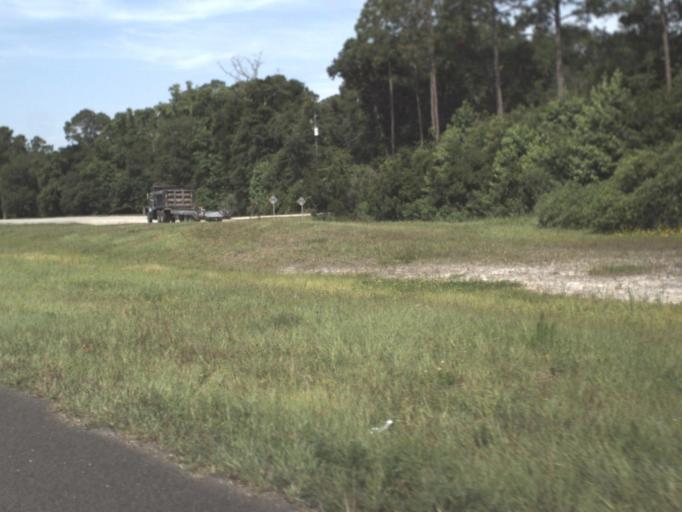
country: US
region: Florida
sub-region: Putnam County
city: East Palatka
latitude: 29.7445
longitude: -81.4721
